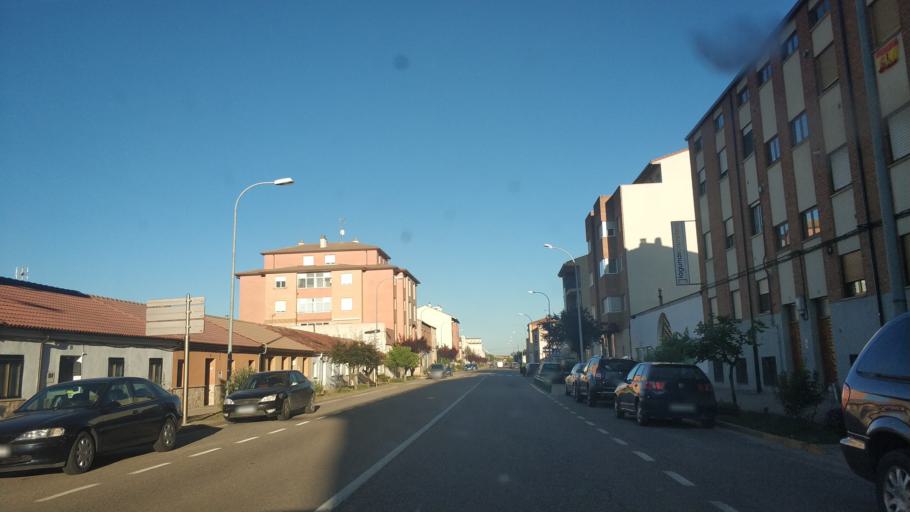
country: ES
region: Castille and Leon
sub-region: Provincia de Soria
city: San Esteban de Gormaz
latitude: 41.5723
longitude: -3.1990
